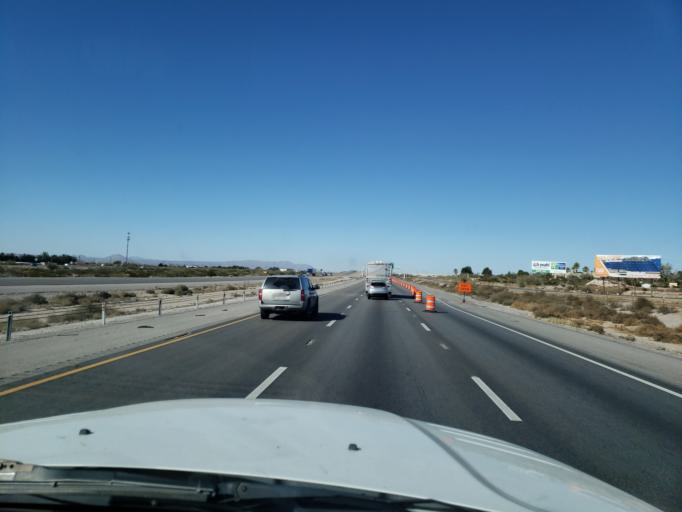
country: US
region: New Mexico
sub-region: Dona Ana County
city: University Park
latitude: 32.2517
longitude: -106.7255
